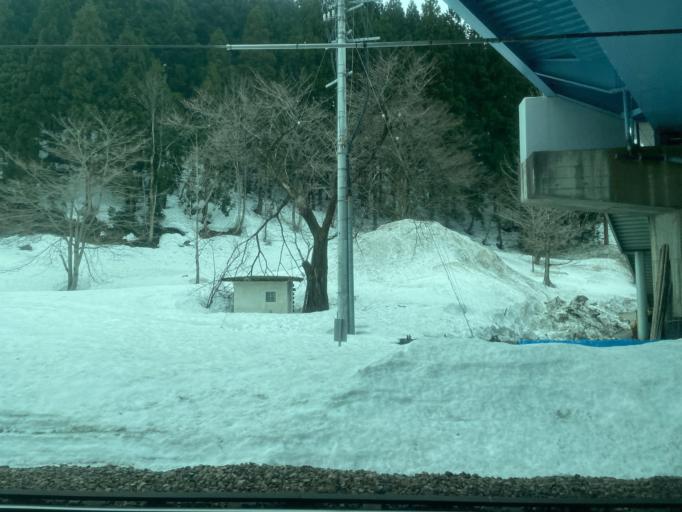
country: JP
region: Niigata
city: Shiozawa
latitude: 36.9332
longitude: 138.8140
